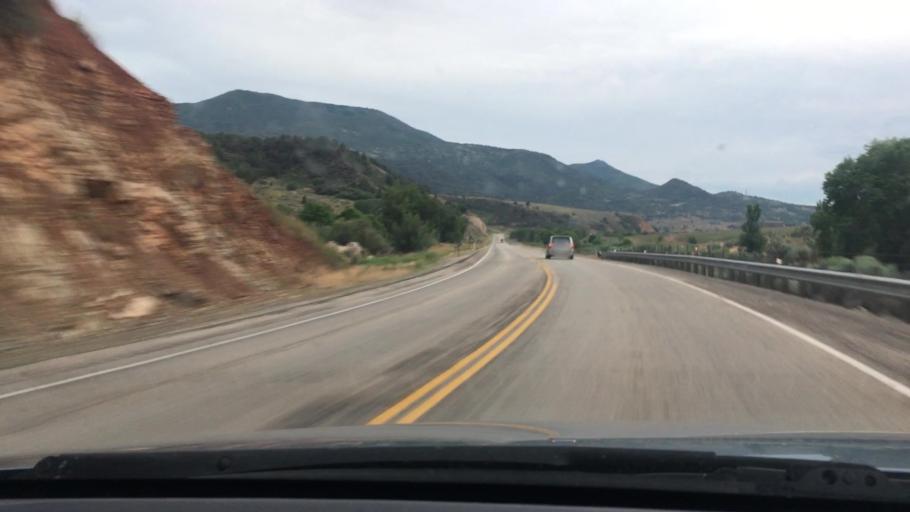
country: US
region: Utah
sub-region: Utah County
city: Woodland Hills
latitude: 39.9843
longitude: -111.5023
